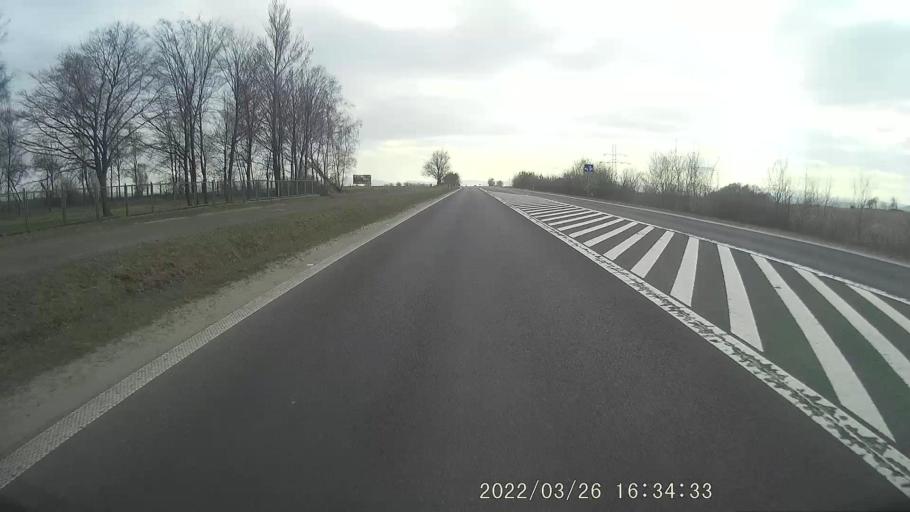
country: DE
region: Saxony
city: Ostritz
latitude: 51.0030
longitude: 14.9491
